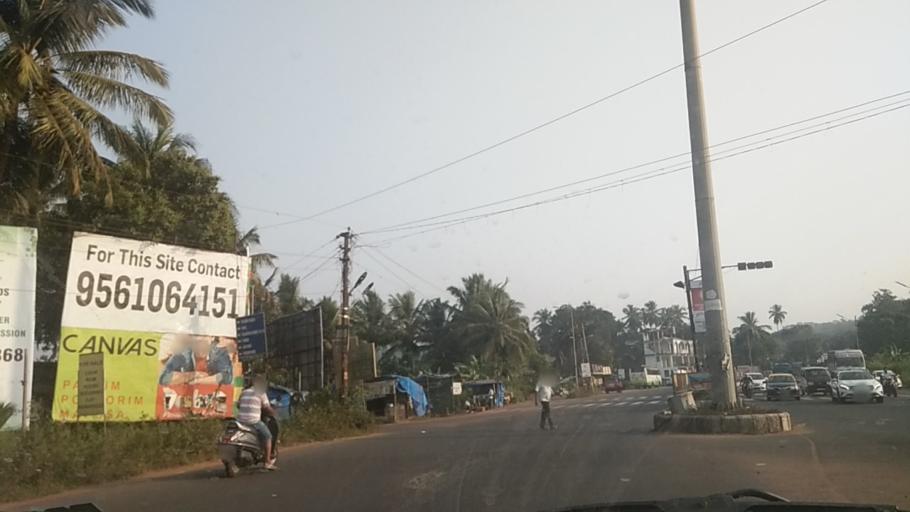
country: IN
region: Goa
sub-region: North Goa
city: Guirim
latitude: 15.5528
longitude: 73.8174
